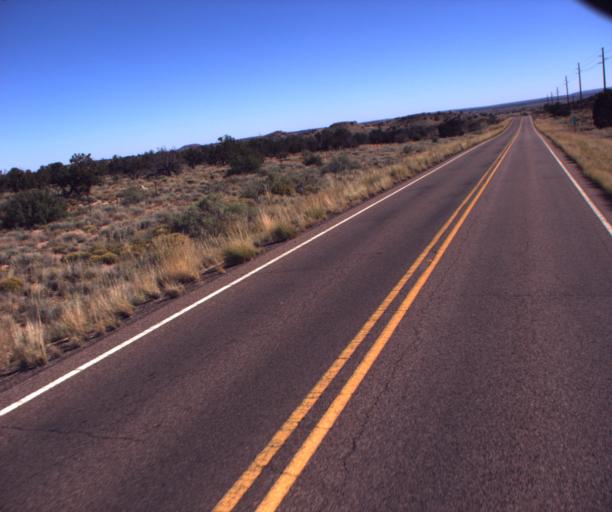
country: US
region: Arizona
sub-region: Navajo County
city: Taylor
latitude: 34.5096
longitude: -110.1750
